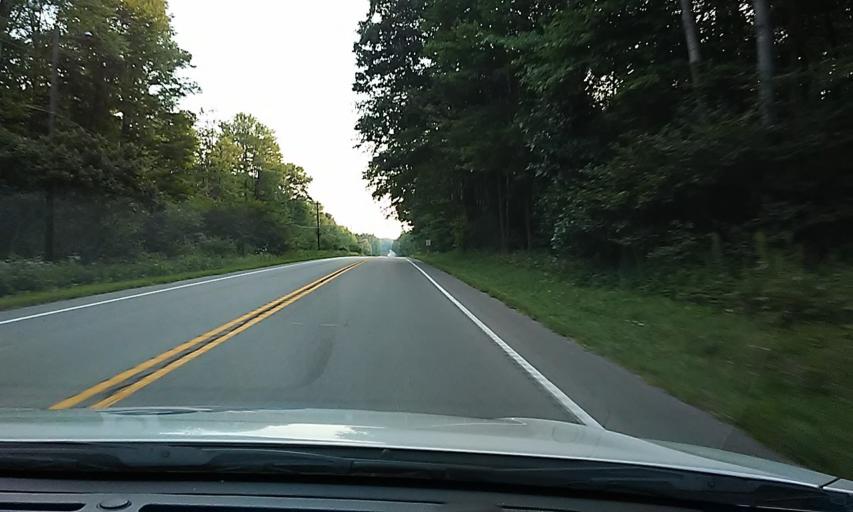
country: US
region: Pennsylvania
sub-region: Forest County
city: Marienville
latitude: 41.4293
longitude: -79.1923
